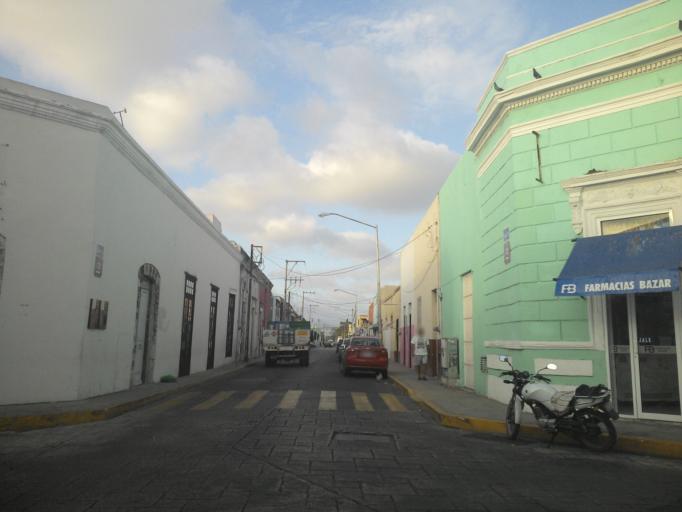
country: MX
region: Yucatan
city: Merida
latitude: 20.9709
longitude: -89.6301
